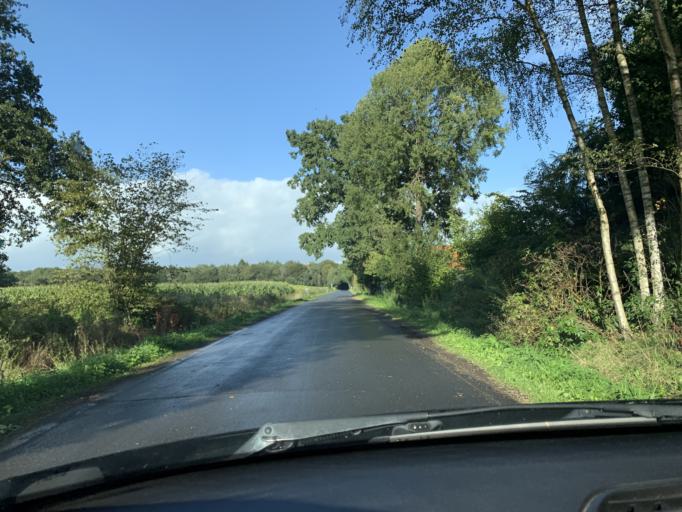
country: DE
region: Lower Saxony
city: Westerstede
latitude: 53.1977
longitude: 7.9116
